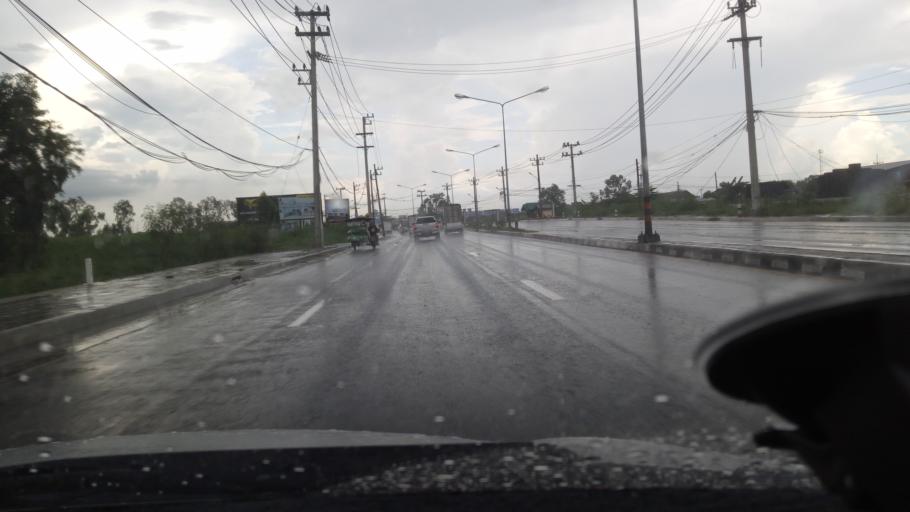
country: TH
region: Chon Buri
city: Phan Thong
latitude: 13.4435
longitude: 101.1037
